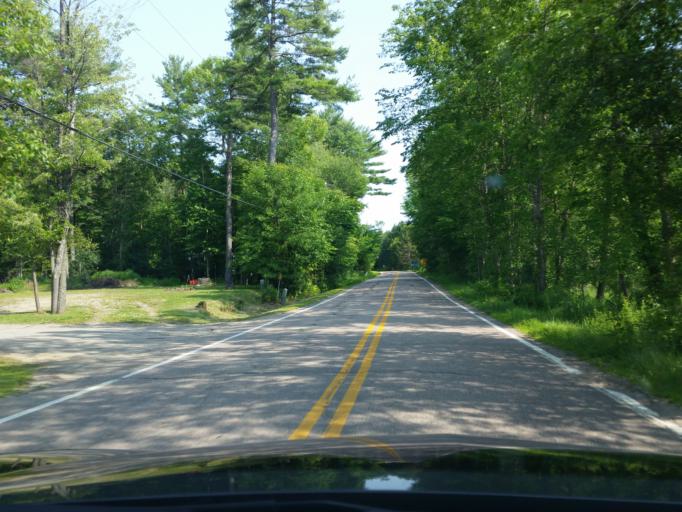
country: CA
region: Quebec
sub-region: Outaouais
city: Shawville
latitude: 45.5283
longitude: -76.4557
